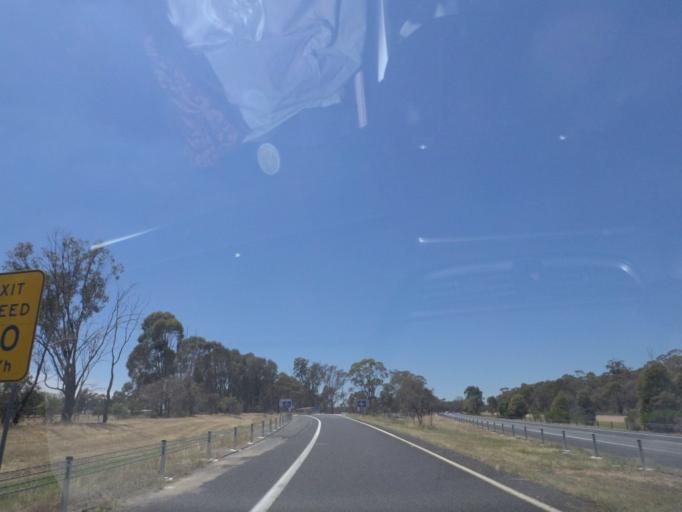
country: AU
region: Victoria
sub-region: Benalla
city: Benalla
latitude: -36.5758
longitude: 145.9279
